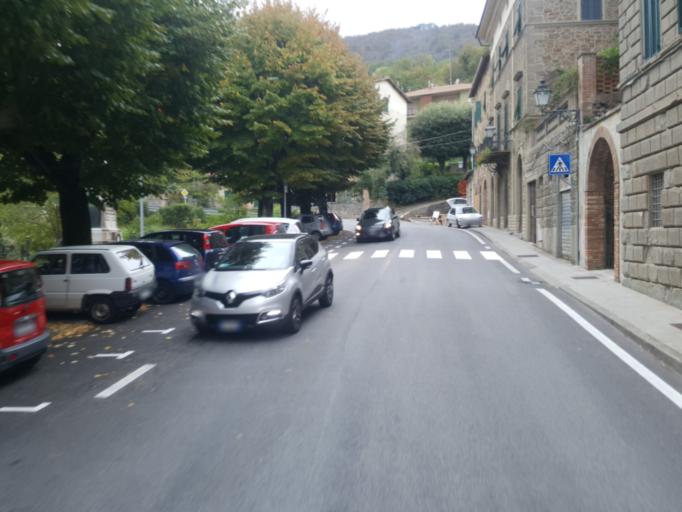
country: IT
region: Tuscany
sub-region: Province of Pisa
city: Castelnuovo di Val di Cecina
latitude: 43.2068
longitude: 10.9059
